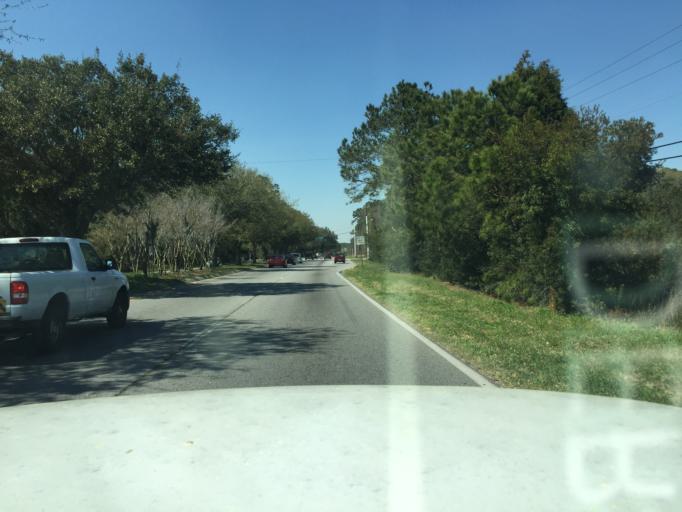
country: US
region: Georgia
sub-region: Chatham County
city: Whitemarsh Island
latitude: 32.0257
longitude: -80.9988
